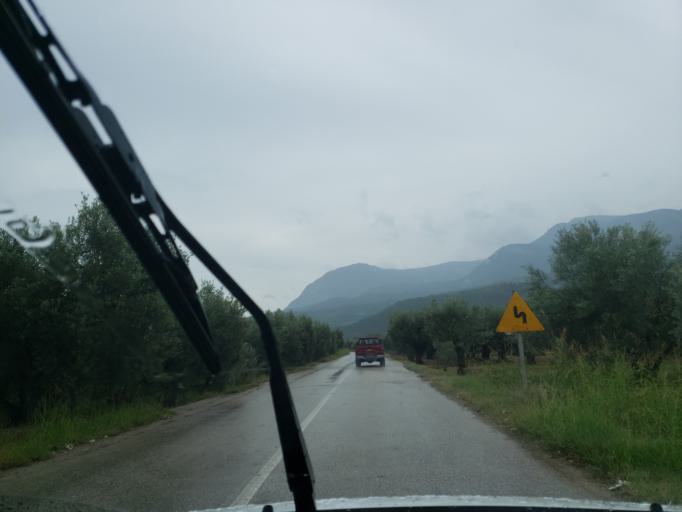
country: GR
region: Central Greece
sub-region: Nomos Fthiotidos
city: Anthili
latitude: 38.8030
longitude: 22.4569
